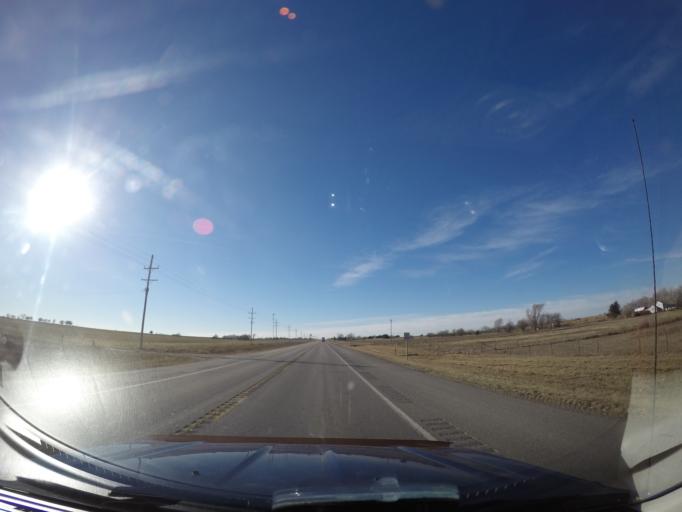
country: US
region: Kansas
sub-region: Marion County
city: Hillsboro
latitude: 38.3627
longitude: -97.2287
